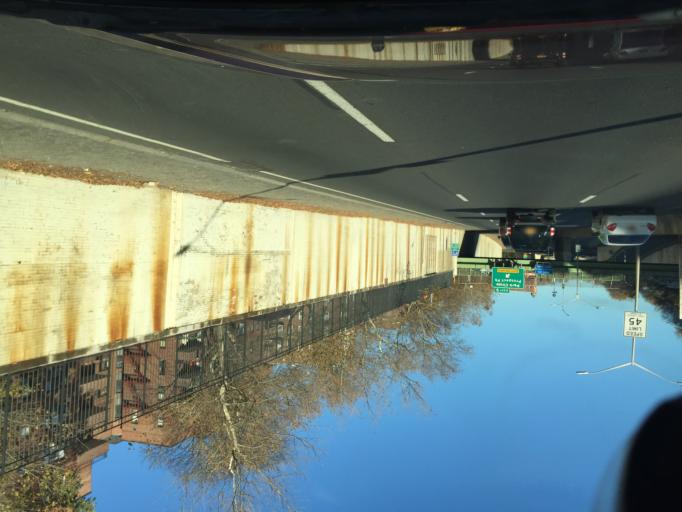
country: US
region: New York
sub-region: Kings County
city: Brooklyn
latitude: 40.6467
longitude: -73.9747
